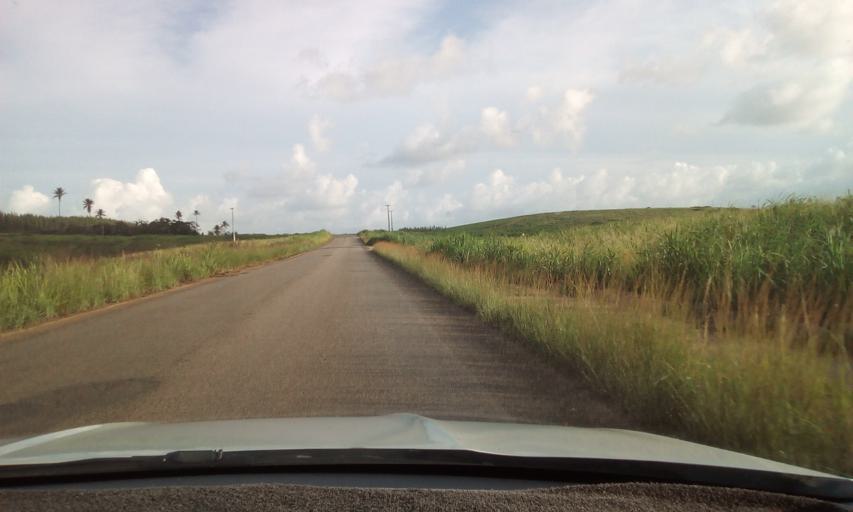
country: BR
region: Pernambuco
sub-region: Gloria Do Goita
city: Gloria do Goita
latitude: -7.9923
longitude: -35.2296
